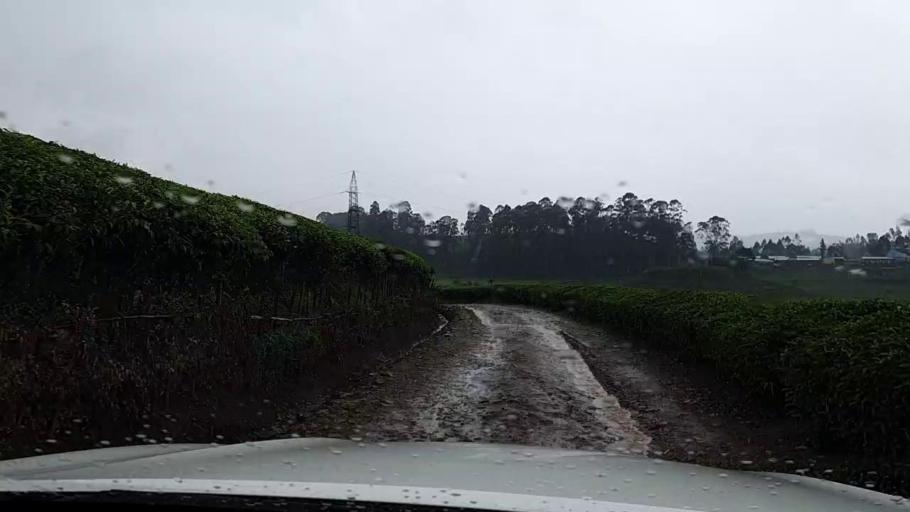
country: RW
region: Western Province
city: Cyangugu
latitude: -2.4534
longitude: 29.0400
